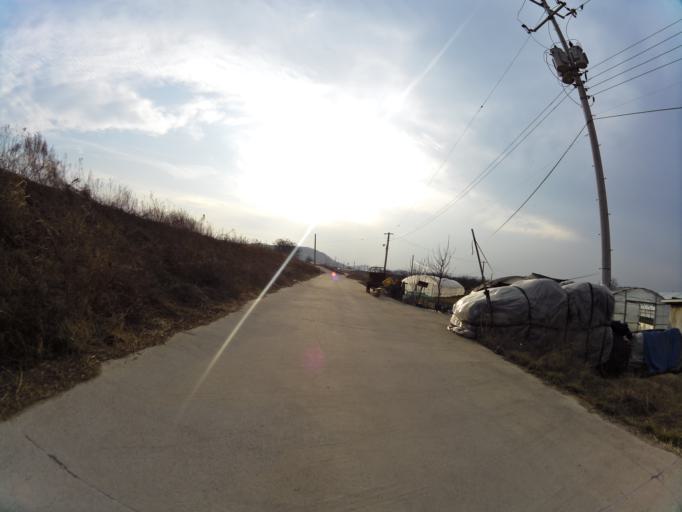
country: KR
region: Gyeongsangbuk-do
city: Gyeongsan-si
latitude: 35.8561
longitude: 128.7144
